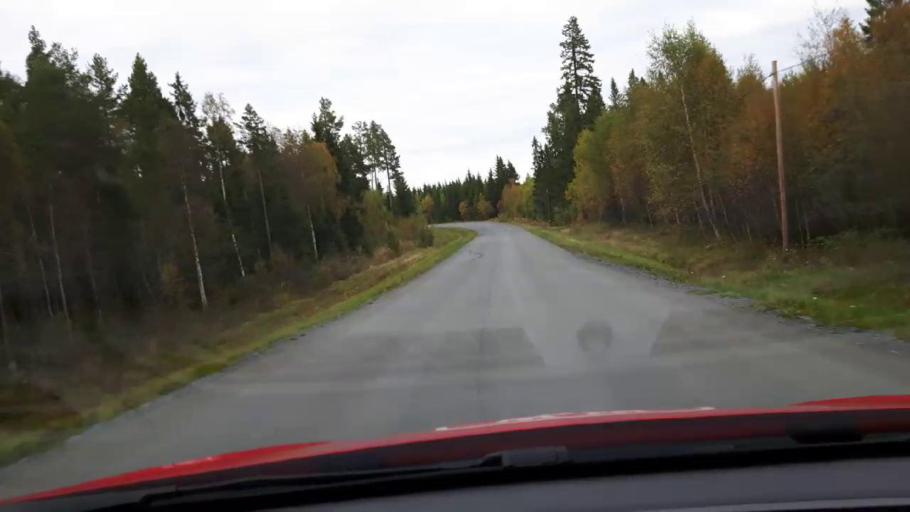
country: SE
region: Jaemtland
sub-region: Krokoms Kommun
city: Krokom
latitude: 63.2212
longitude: 14.1298
